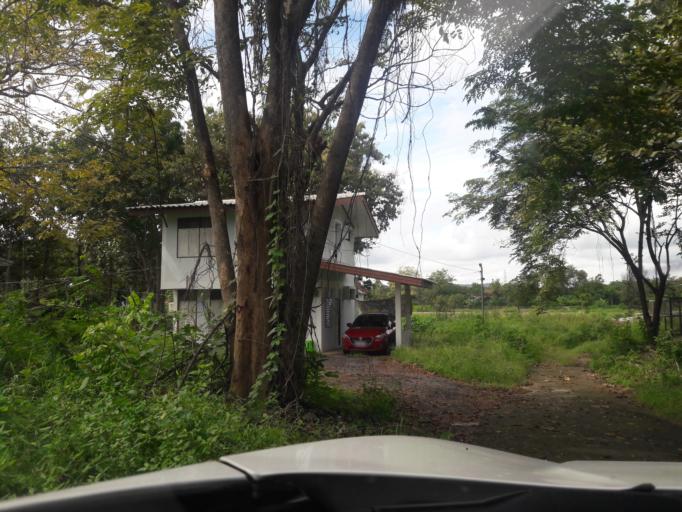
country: TH
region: Nakhon Sawan
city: Tak Fa
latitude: 15.3474
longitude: 100.4911
